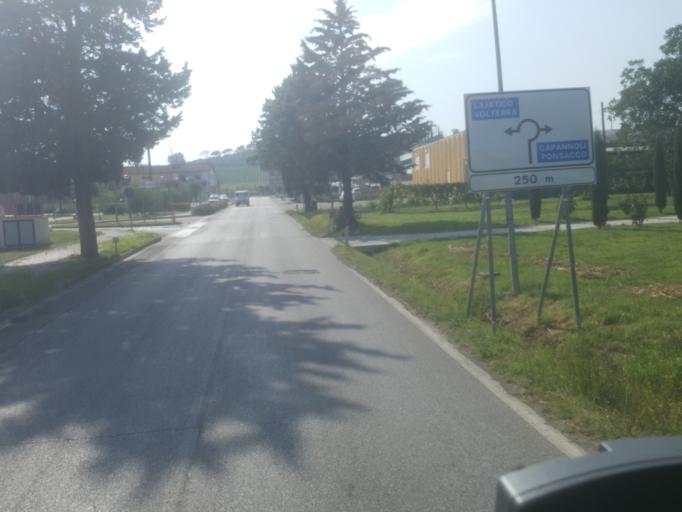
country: IT
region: Tuscany
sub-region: Province of Pisa
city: Peccioli
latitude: 43.5421
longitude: 10.7027
